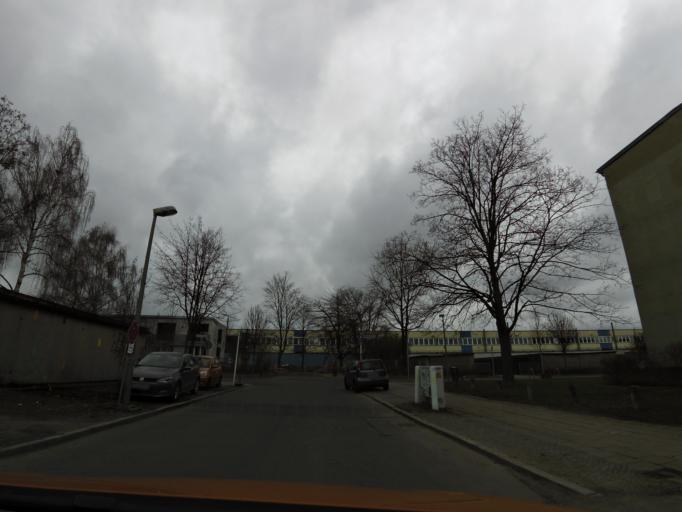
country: DE
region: Berlin
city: Lichtenberg
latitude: 52.5179
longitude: 13.5026
